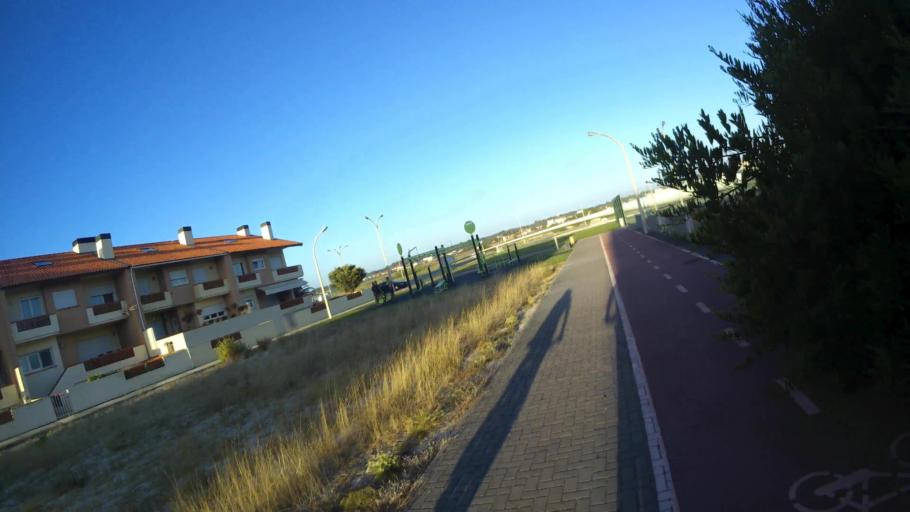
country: PT
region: Aveiro
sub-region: Ilhavo
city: Gafanha da Encarnacao
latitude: 40.5628
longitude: -8.7596
